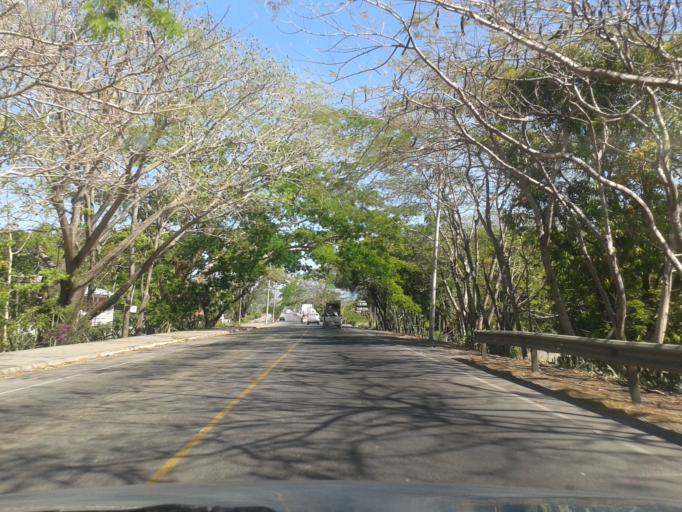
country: CR
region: Puntarenas
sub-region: Canton Central de Puntarenas
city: Chacarita
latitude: 9.9614
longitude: -84.7360
